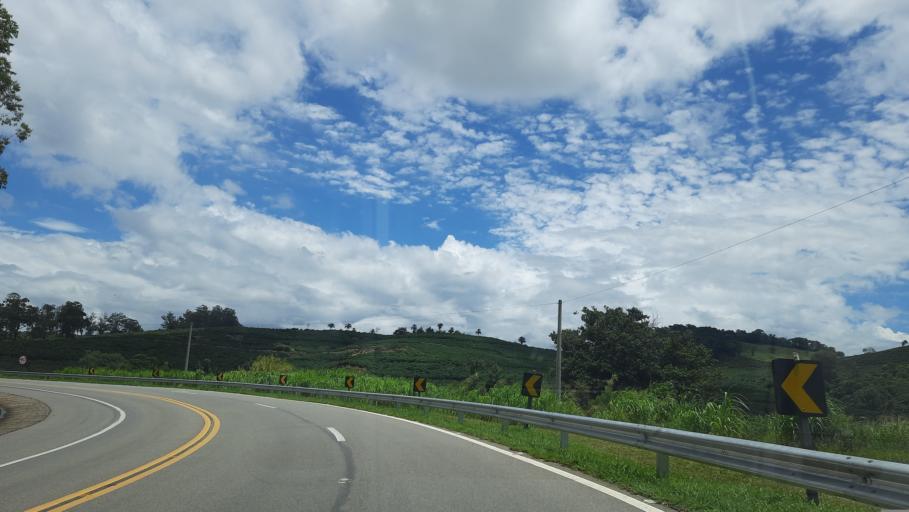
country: BR
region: Sao Paulo
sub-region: Vargem Grande Do Sul
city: Vargem Grande do Sul
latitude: -21.7995
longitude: -46.8201
